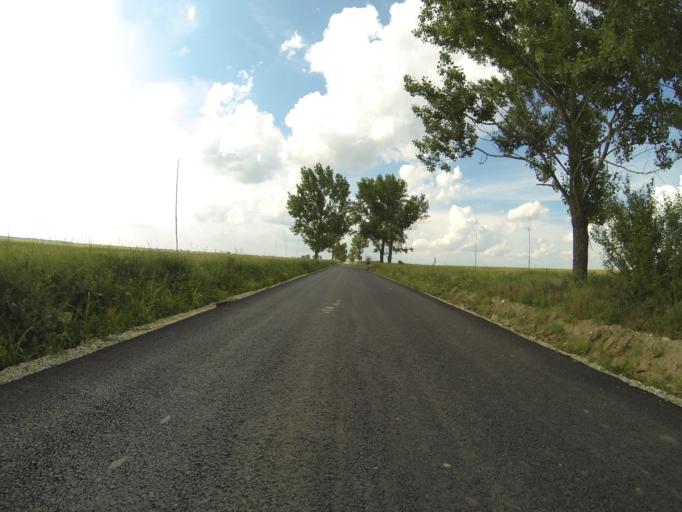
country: RO
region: Dolj
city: Satu Nou Calopar
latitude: 44.1381
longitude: 23.7950
